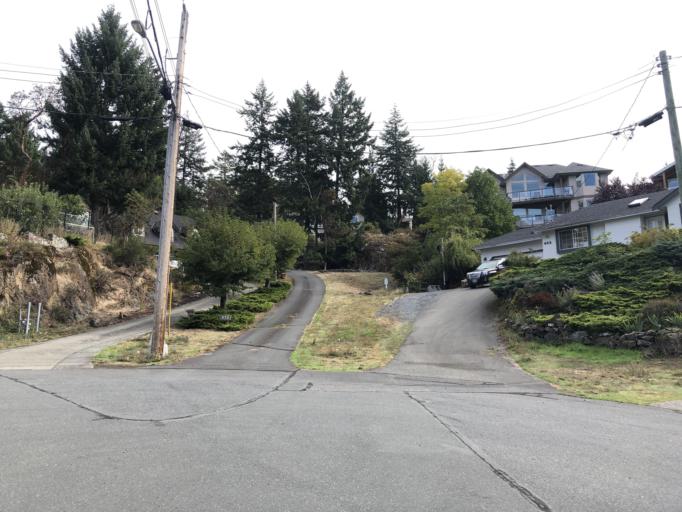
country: CA
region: British Columbia
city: Langford
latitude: 48.4705
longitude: -123.4964
